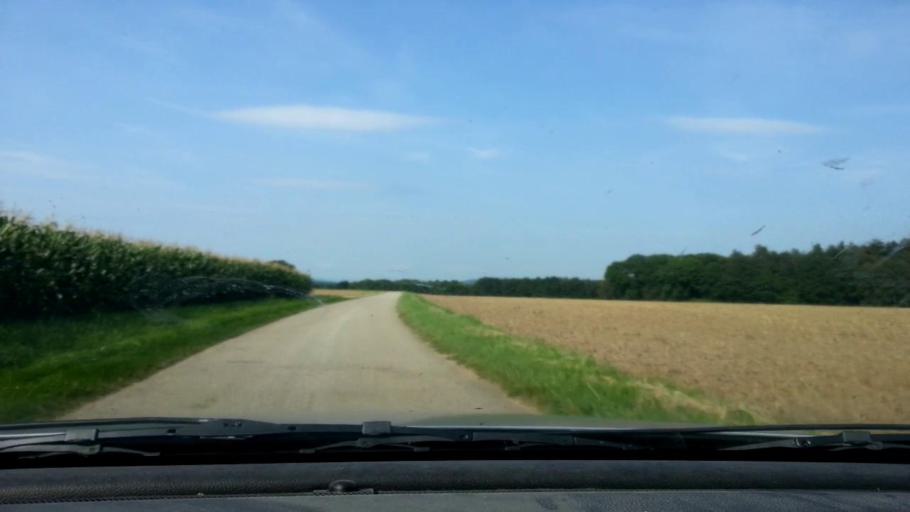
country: DE
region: Bavaria
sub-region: Upper Franconia
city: Zapfendorf
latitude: 49.9914
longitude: 10.9442
